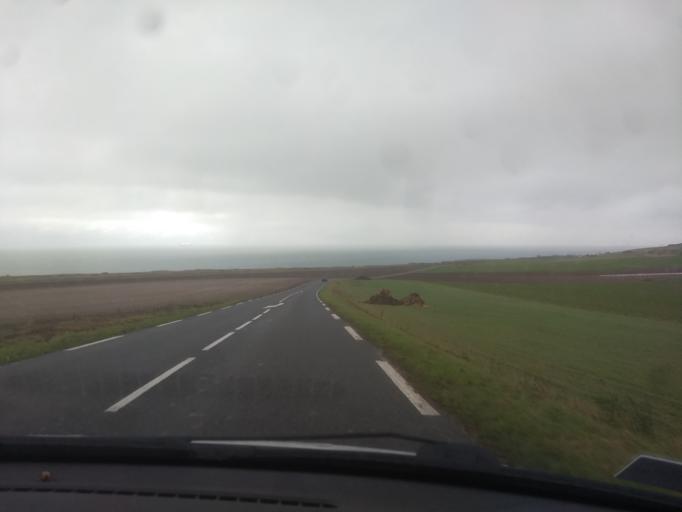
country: FR
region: Nord-Pas-de-Calais
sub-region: Departement du Pas-de-Calais
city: Sangatte
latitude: 50.9309
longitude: 1.7217
